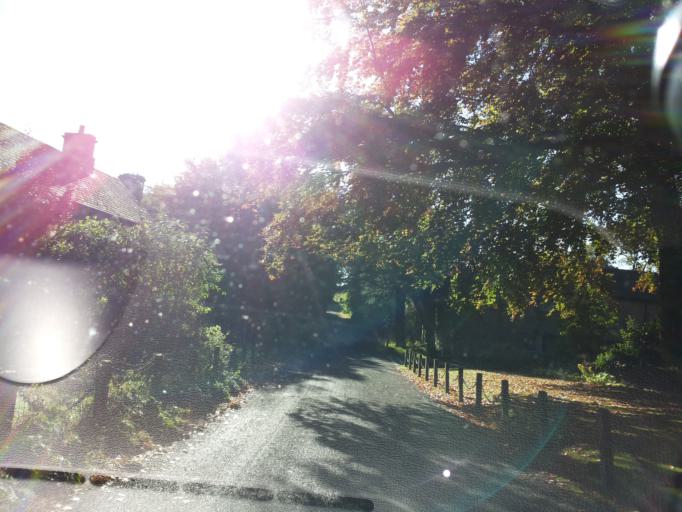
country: GB
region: England
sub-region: North Yorkshire
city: Catterick Garrison
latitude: 54.3992
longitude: -1.7136
